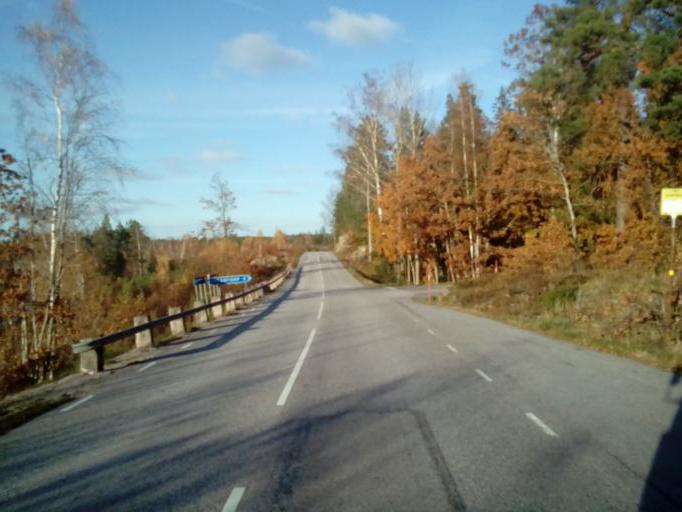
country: SE
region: Kalmar
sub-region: Vasterviks Kommun
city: Ankarsrum
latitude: 57.7400
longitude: 16.1085
